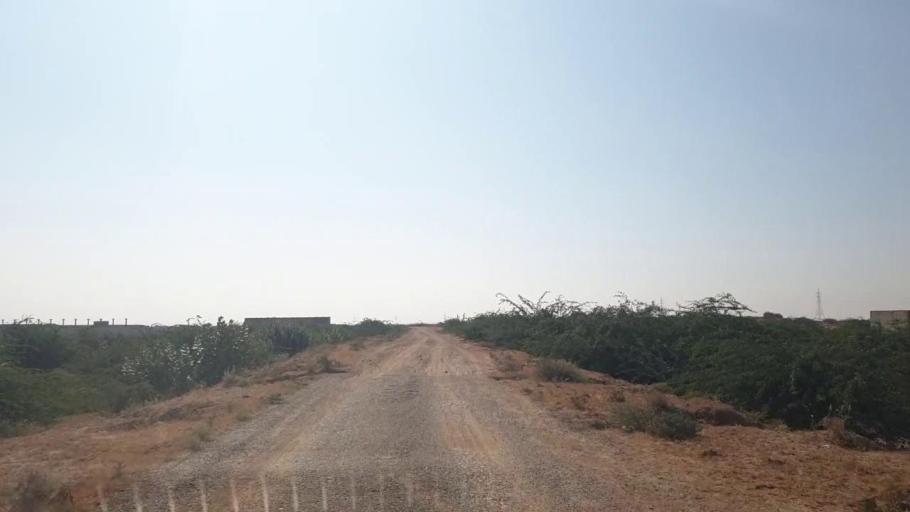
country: PK
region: Sindh
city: Gharo
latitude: 25.1453
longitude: 67.7268
